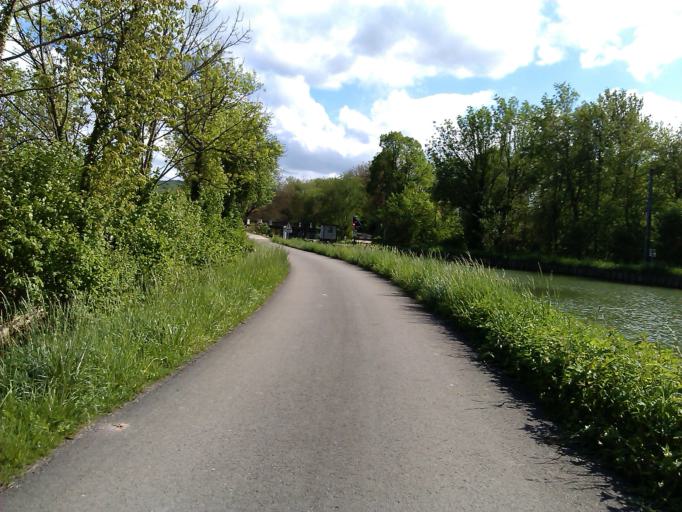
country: FR
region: Franche-Comte
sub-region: Departement du Doubs
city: Colombier-Fontaine
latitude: 47.4394
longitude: 6.6281
